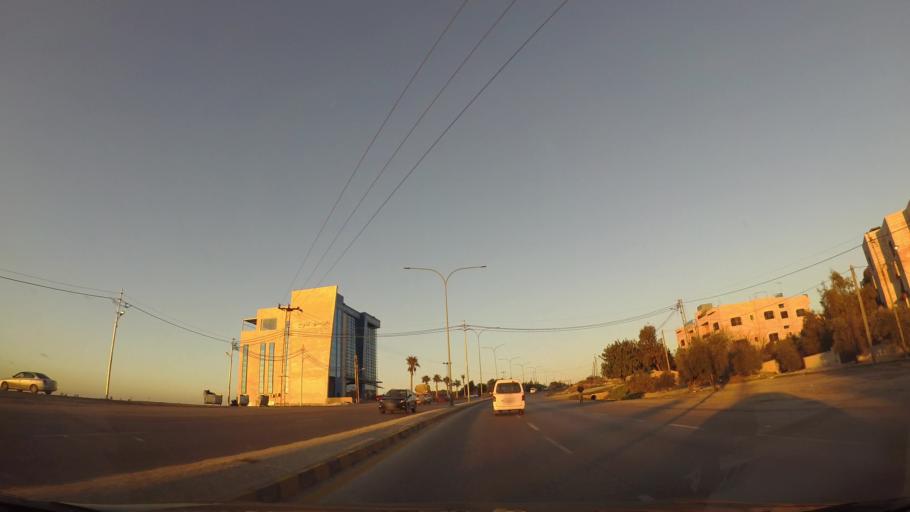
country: JO
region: Amman
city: Umm as Summaq
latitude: 31.8649
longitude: 35.8256
